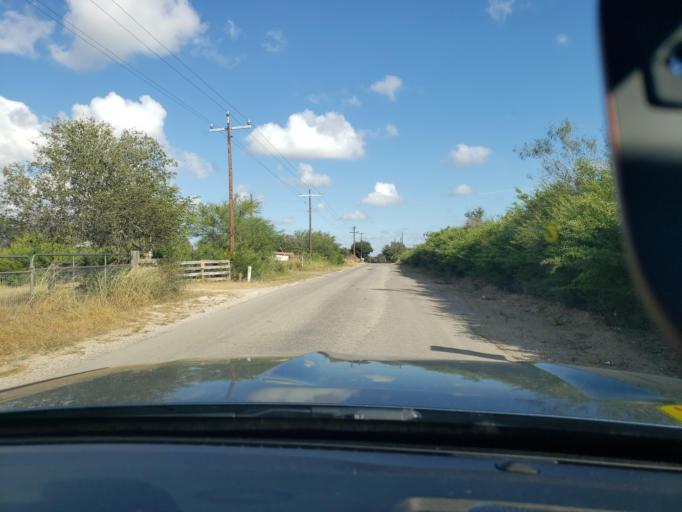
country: US
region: Texas
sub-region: Bee County
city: Beeville
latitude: 28.4575
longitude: -97.7183
